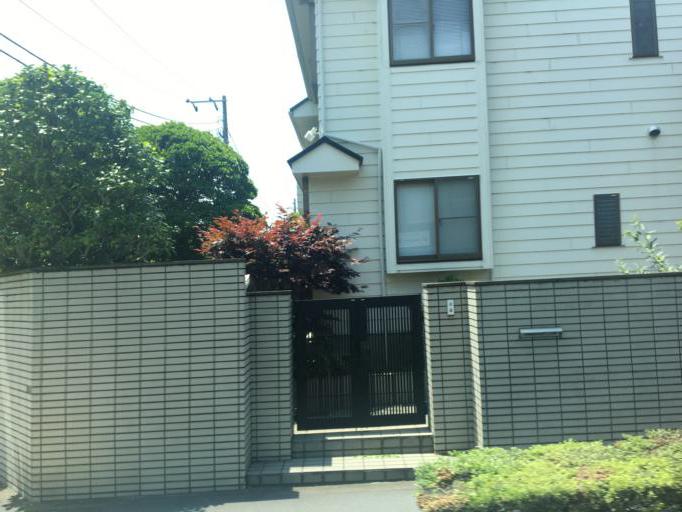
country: JP
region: Saitama
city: Kawaguchi
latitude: 35.7621
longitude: 139.6901
